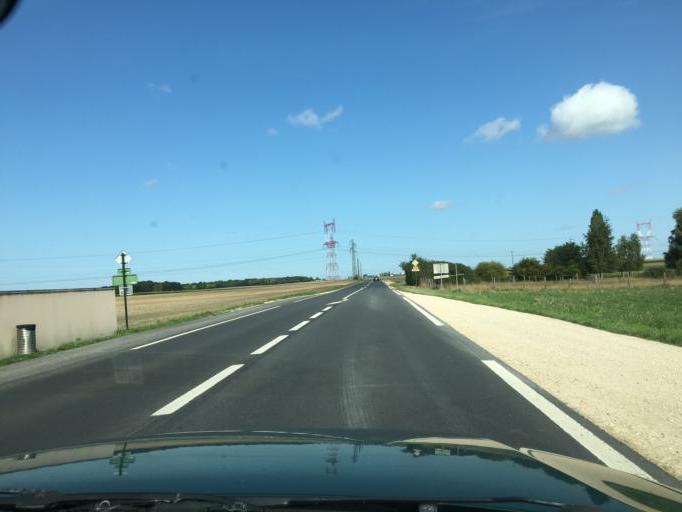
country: FR
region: Centre
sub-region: Departement du Loiret
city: Ormes
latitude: 47.9459
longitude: 1.8124
